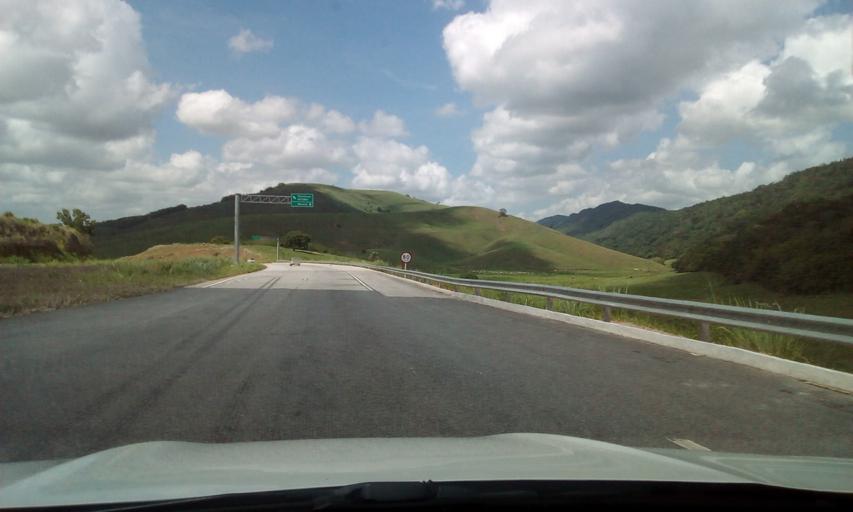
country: BR
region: Alagoas
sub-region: Flexeiras
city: Flexeiras
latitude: -9.2528
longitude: -35.7711
